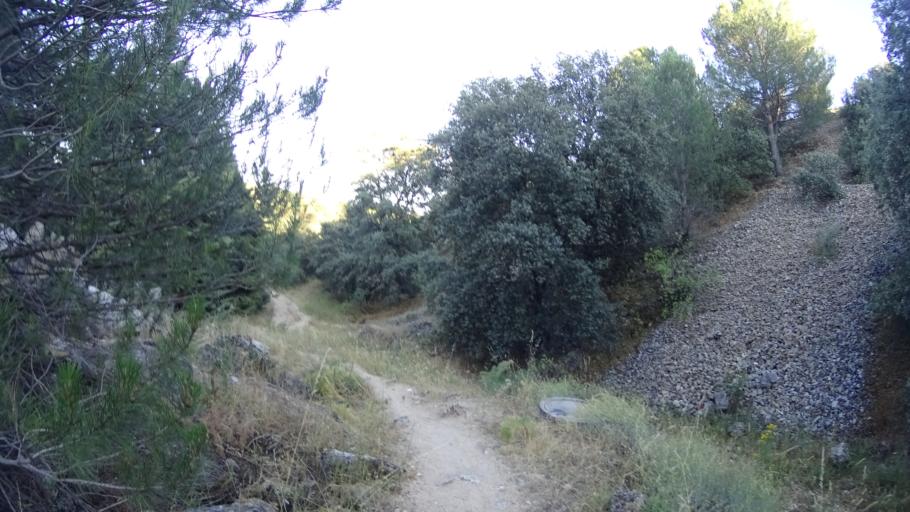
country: ES
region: Madrid
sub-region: Provincia de Madrid
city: Galapagar
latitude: 40.5892
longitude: -3.9668
